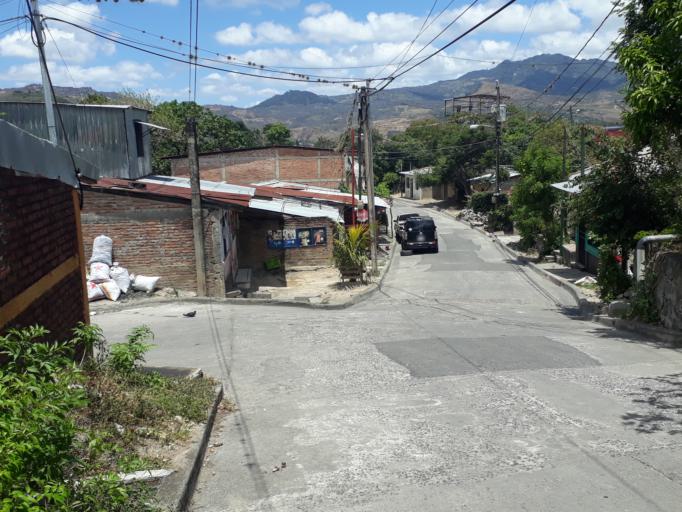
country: NI
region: Matagalpa
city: Matagalpa
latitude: 12.9204
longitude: -85.9140
